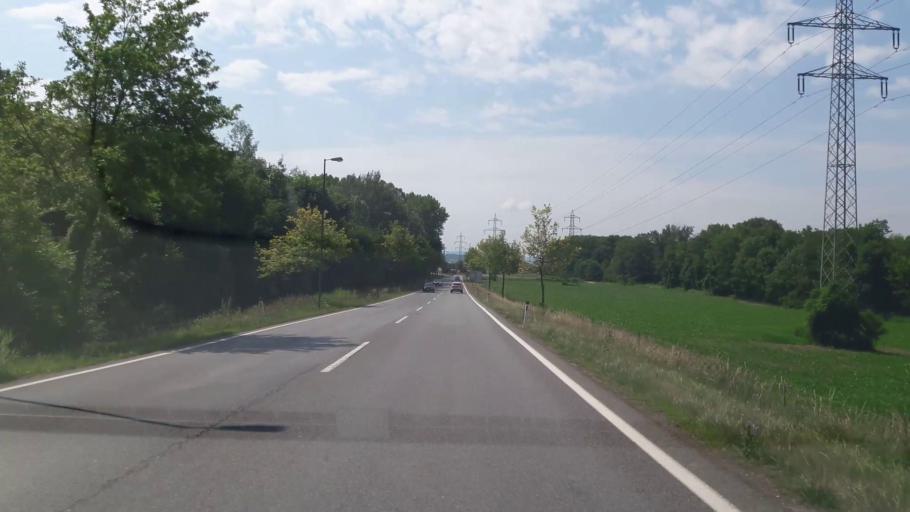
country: AT
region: Lower Austria
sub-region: Politischer Bezirk Tulln
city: Tulln
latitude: 48.3309
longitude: 16.0276
